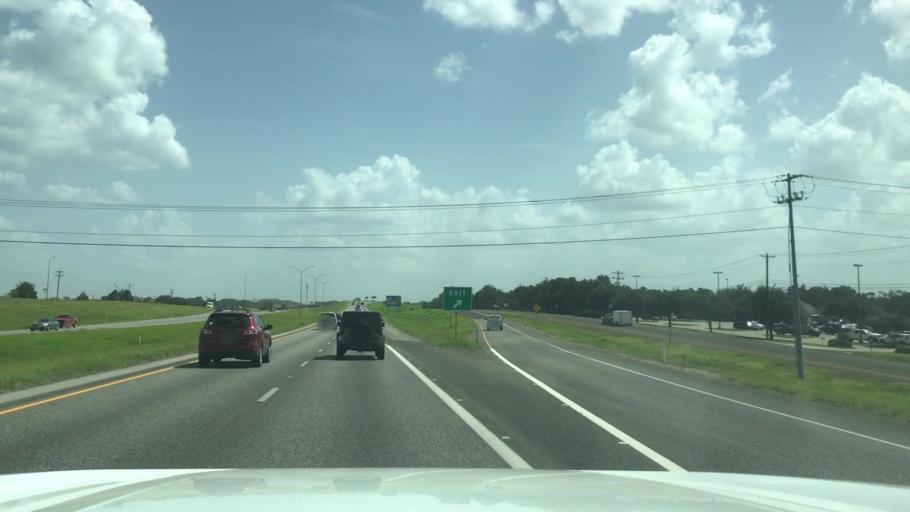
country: US
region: Texas
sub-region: Brazos County
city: College Station
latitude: 30.6015
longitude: -96.2904
